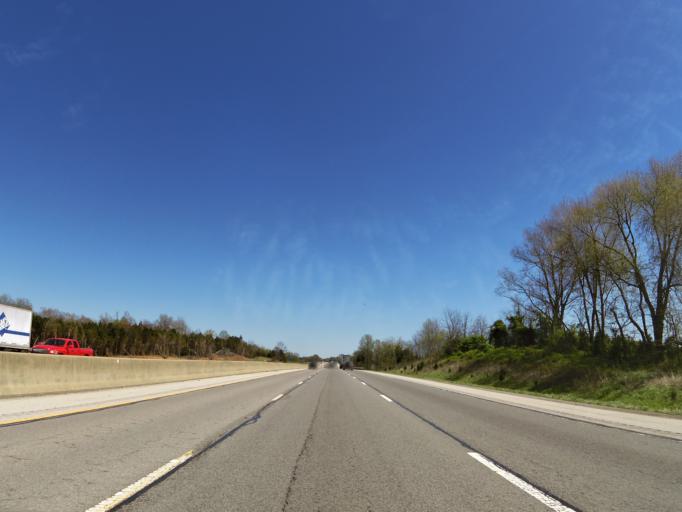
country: US
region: Kentucky
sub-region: Warren County
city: Bowling Green
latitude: 37.0117
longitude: -86.3247
